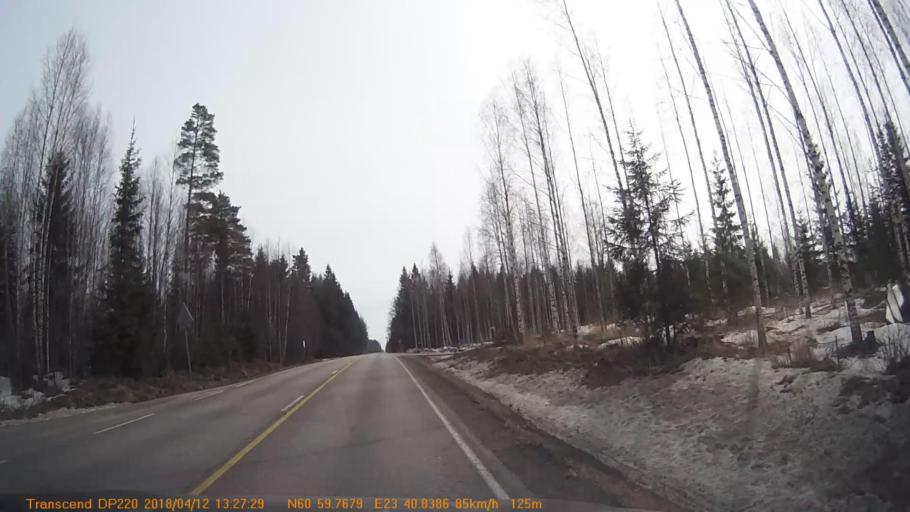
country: FI
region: Pirkanmaa
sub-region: Etelae-Pirkanmaa
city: Kylmaekoski
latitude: 60.9960
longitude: 23.6808
